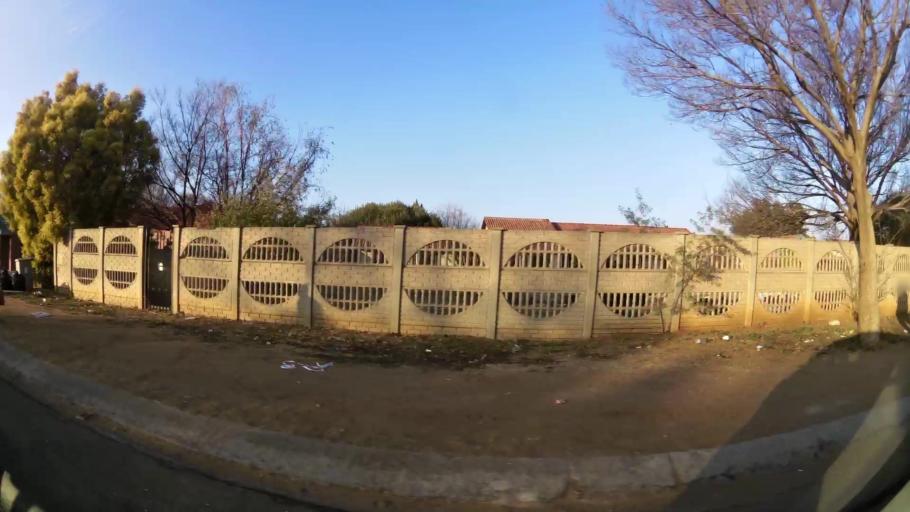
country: ZA
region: Orange Free State
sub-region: Mangaung Metropolitan Municipality
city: Bloemfontein
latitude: -29.1012
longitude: 26.1571
